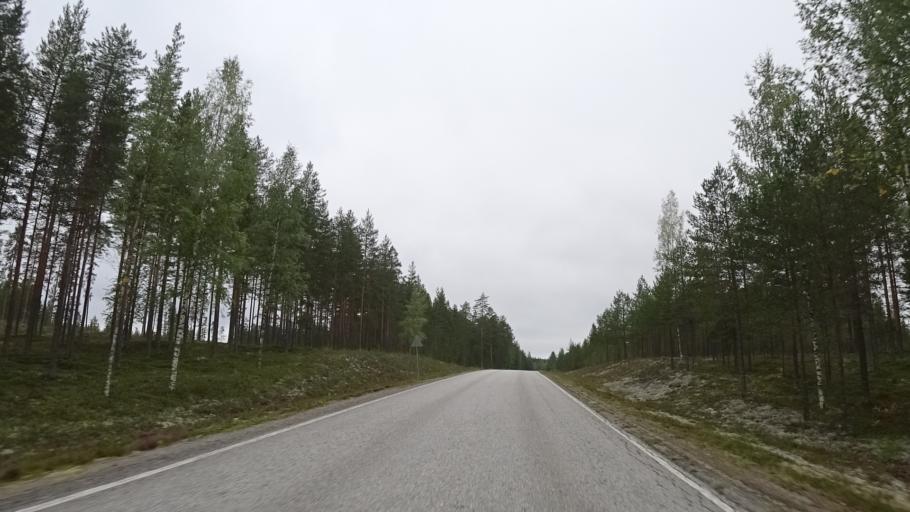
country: FI
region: North Karelia
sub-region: Pielisen Karjala
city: Lieksa
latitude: 63.3405
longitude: 30.2567
